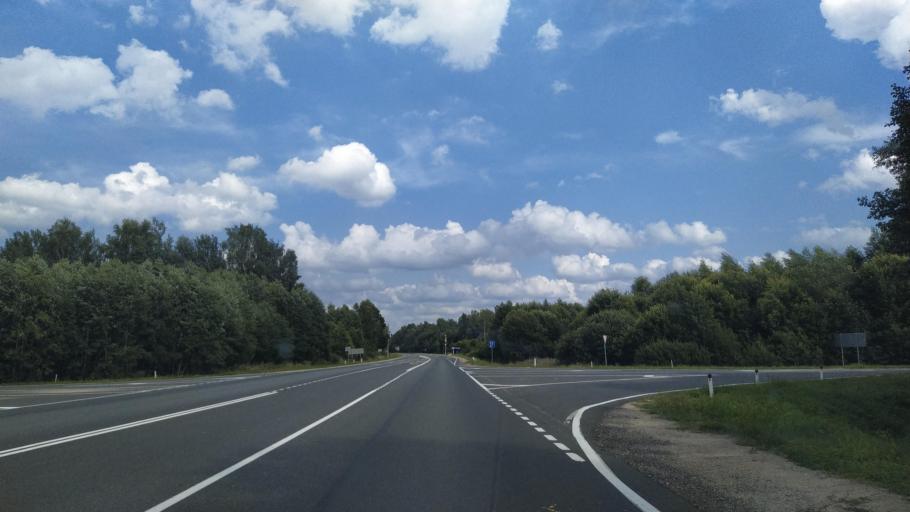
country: RU
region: Pskov
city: Dno
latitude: 57.9932
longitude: 29.8466
